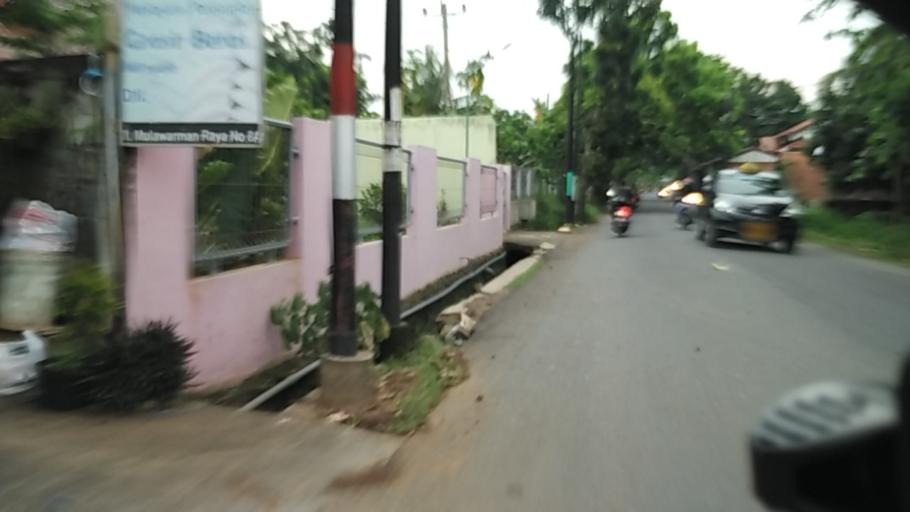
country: ID
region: Central Java
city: Semarang
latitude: -7.0684
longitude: 110.4344
